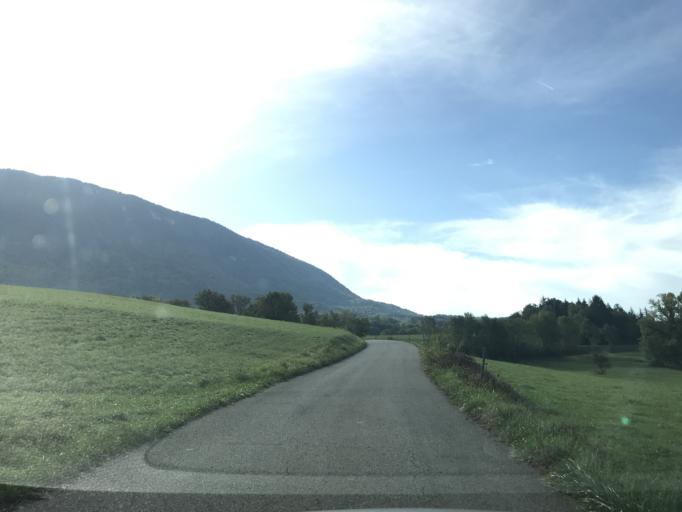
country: FR
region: Rhone-Alpes
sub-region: Departement de la Savoie
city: Yenne
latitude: 45.6863
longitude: 5.7956
